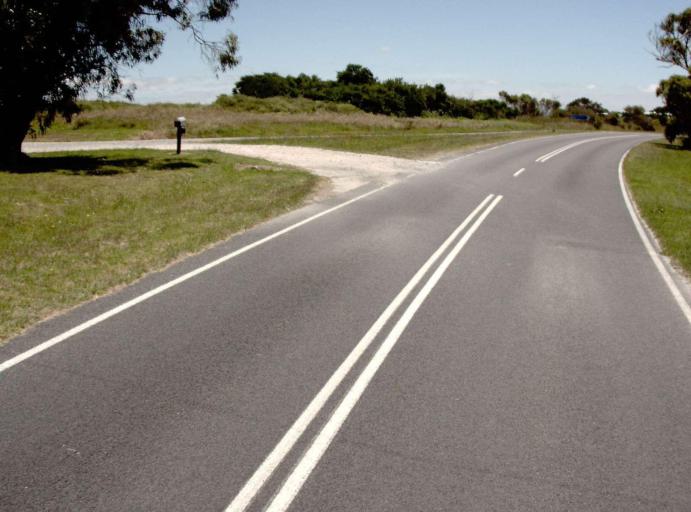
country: AU
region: Victoria
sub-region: Latrobe
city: Morwell
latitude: -38.8455
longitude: 146.2416
